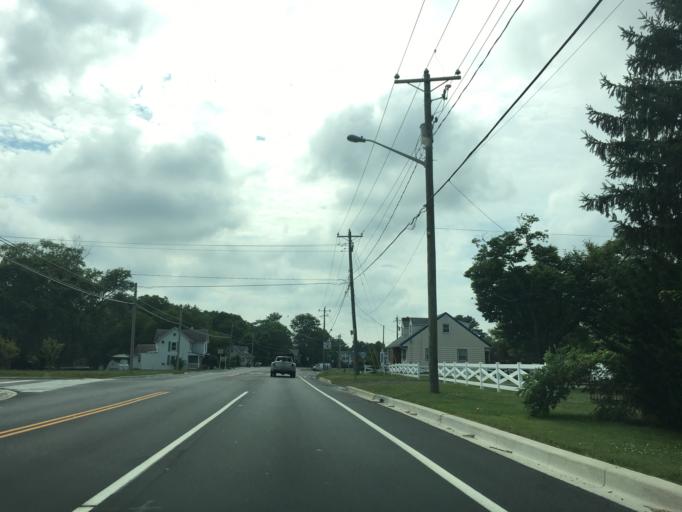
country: US
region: Delaware
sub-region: Sussex County
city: Ocean View
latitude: 38.5480
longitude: -75.1148
